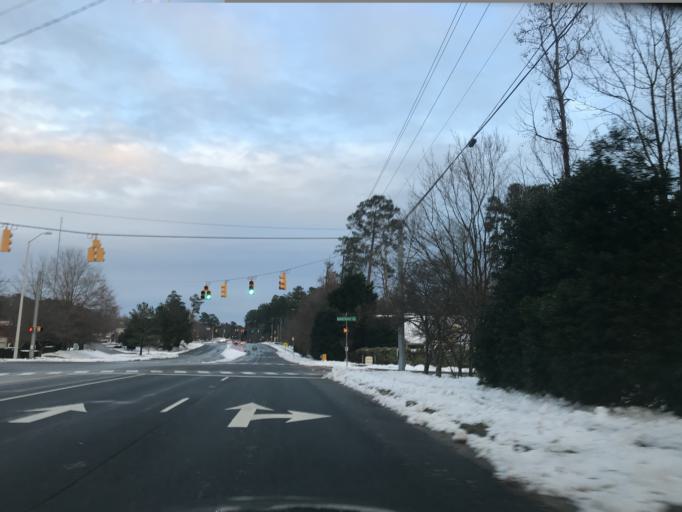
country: US
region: North Carolina
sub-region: Wake County
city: Wake Forest
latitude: 35.9054
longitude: -78.5914
